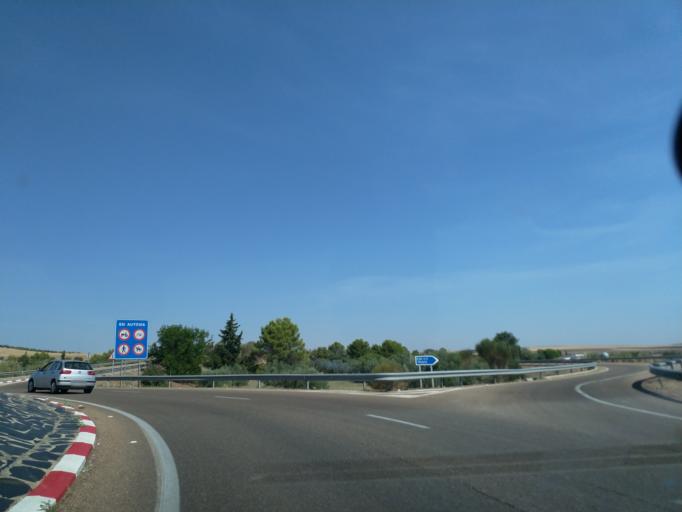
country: ES
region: Extremadura
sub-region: Provincia de Badajoz
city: Merida
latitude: 38.9401
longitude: -6.3430
